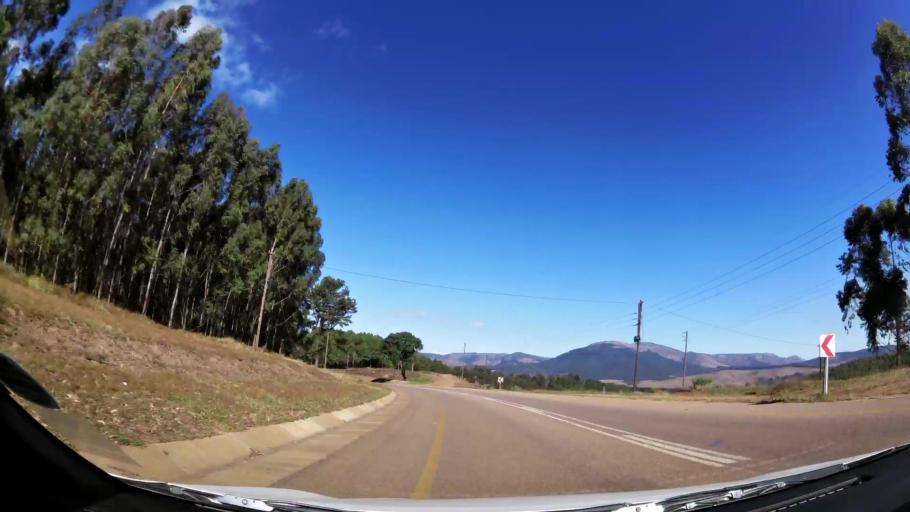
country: ZA
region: Limpopo
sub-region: Capricorn District Municipality
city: Mankoeng
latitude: -23.9211
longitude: 29.9582
